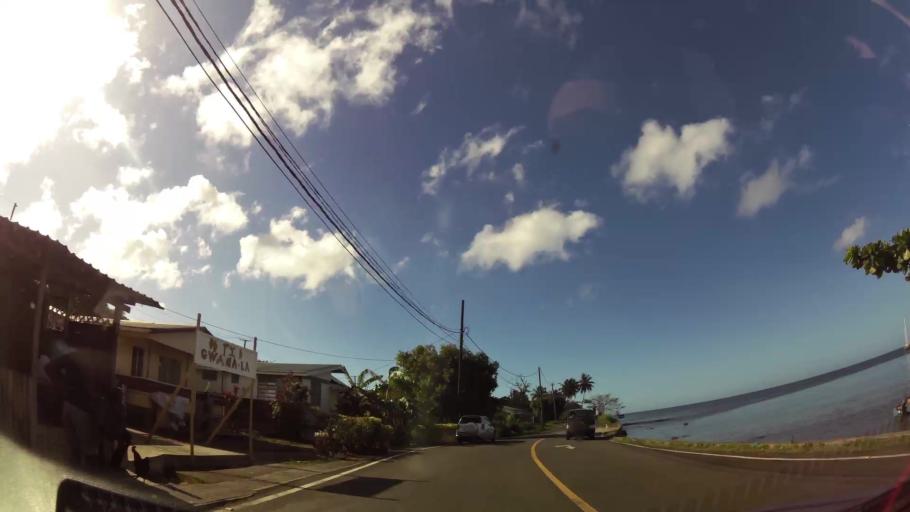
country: DM
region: Saint John
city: Portsmouth
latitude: 15.5683
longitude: -61.4567
